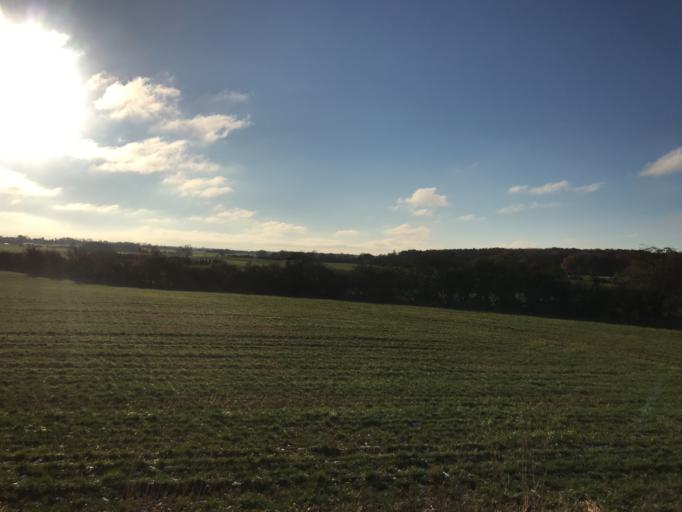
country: DK
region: Zealand
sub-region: Stevns Kommune
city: Harlev
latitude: 55.3792
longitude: 12.2032
